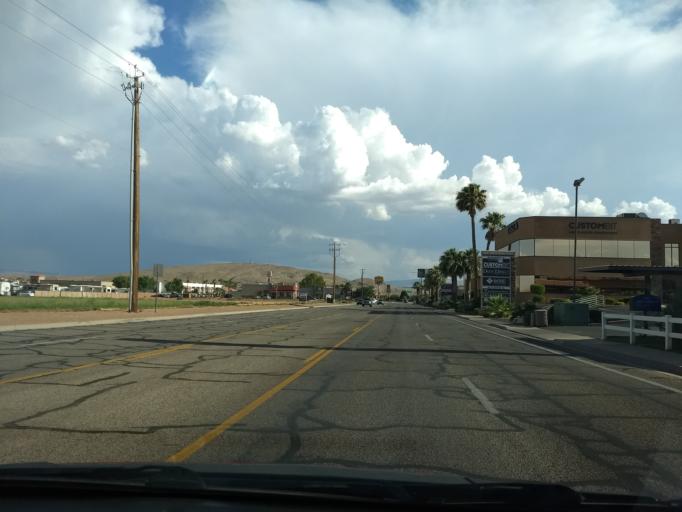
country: US
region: Utah
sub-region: Washington County
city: Saint George
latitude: 37.0905
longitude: -113.5835
